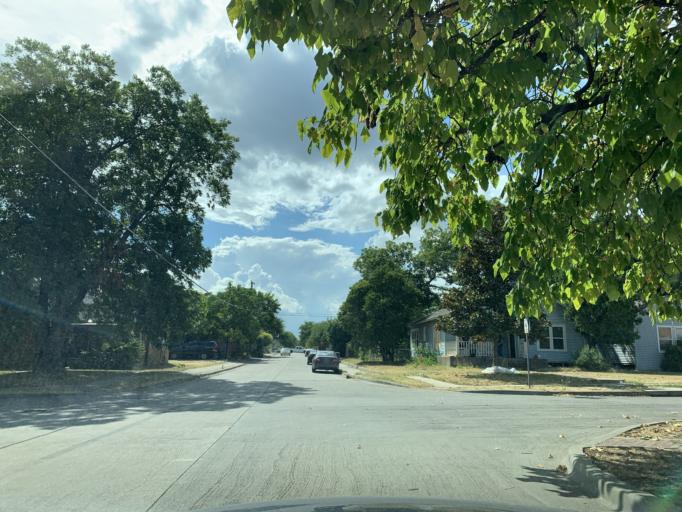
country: US
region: Texas
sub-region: Dallas County
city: Cockrell Hill
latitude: 32.7481
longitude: -96.8726
